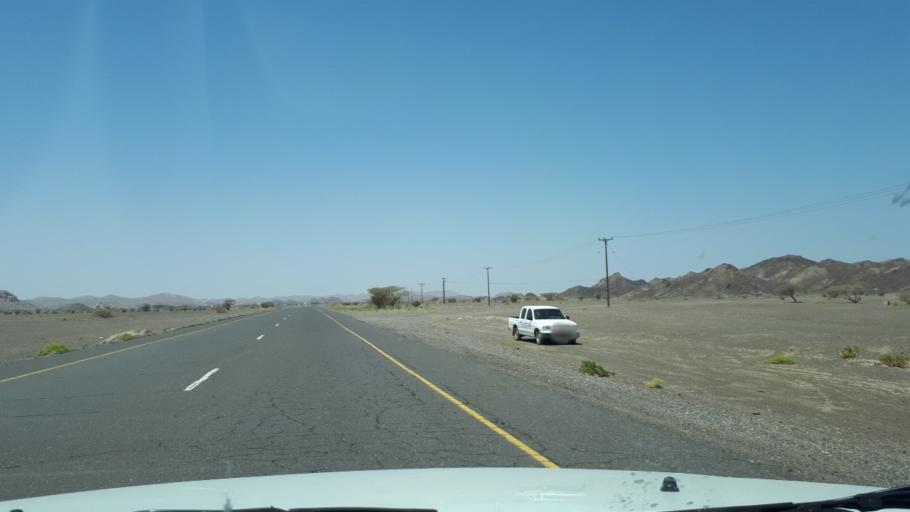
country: OM
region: Ash Sharqiyah
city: Ibra'
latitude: 22.6229
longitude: 58.4488
